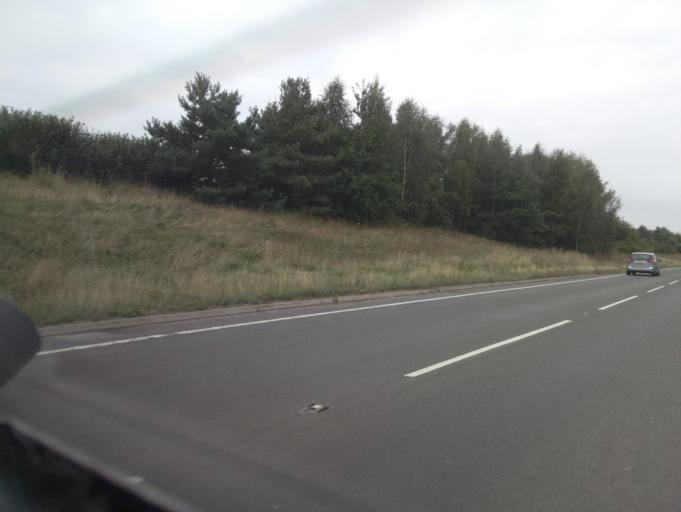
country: GB
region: England
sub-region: Shropshire
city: Stoke upon Tern
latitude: 52.8426
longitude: -2.5781
